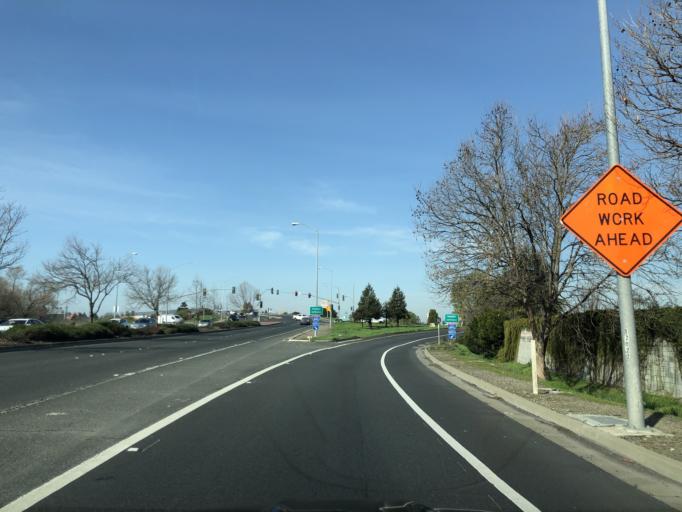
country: US
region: California
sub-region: Alameda County
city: Union City
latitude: 37.5976
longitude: -122.0577
